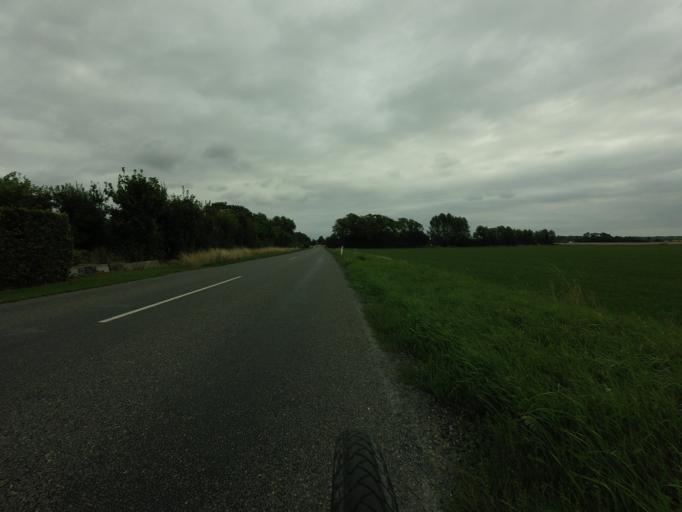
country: DK
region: Zealand
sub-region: Stevns Kommune
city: Store Heddinge
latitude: 55.3449
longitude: 12.3330
